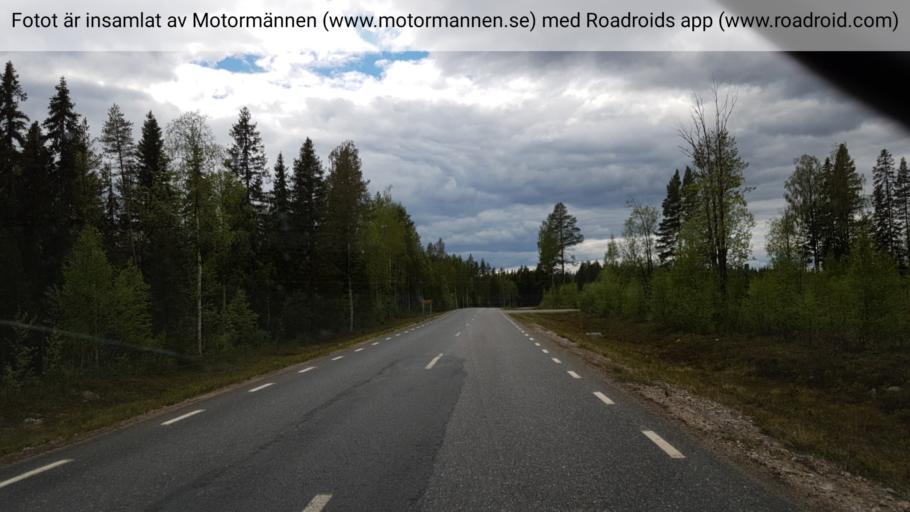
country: SE
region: Vaesterbotten
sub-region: Vindelns Kommun
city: Vindeln
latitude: 64.5271
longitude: 19.8573
